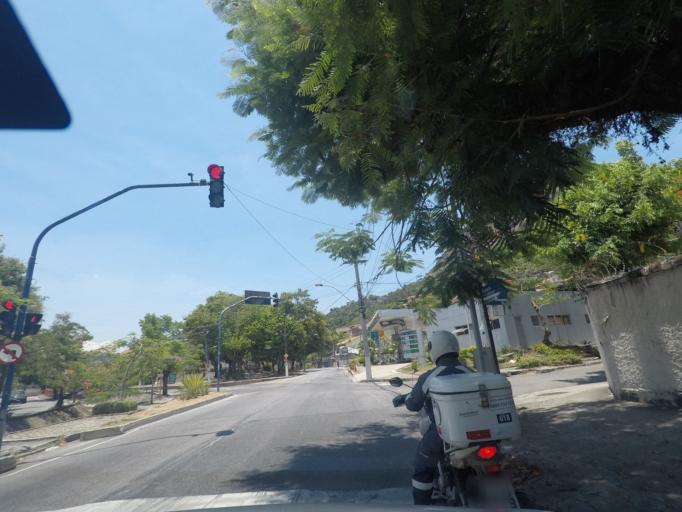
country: BR
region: Rio de Janeiro
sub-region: Niteroi
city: Niteroi
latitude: -22.9140
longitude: -43.0830
